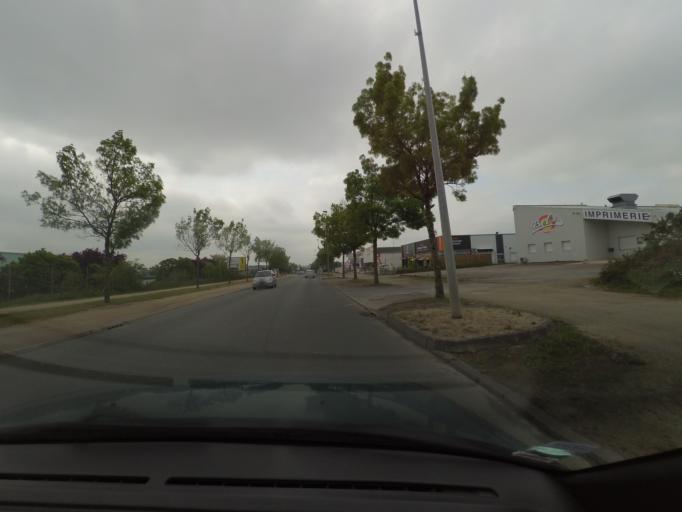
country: FR
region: Pays de la Loire
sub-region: Departement de la Vendee
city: La Roche-sur-Yon
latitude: 46.6551
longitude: -1.4393
